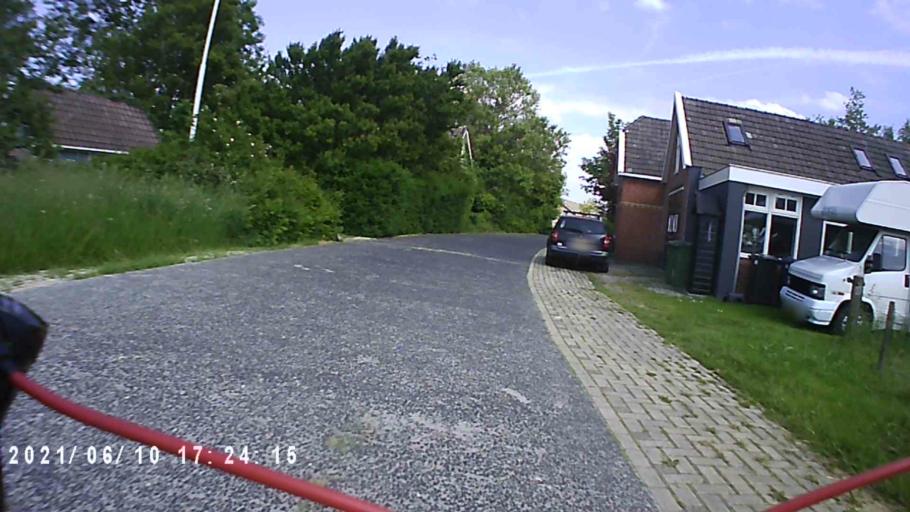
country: NL
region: Friesland
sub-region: Gemeente Kollumerland en Nieuwkruisland
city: Kollum
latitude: 53.2971
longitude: 6.2271
